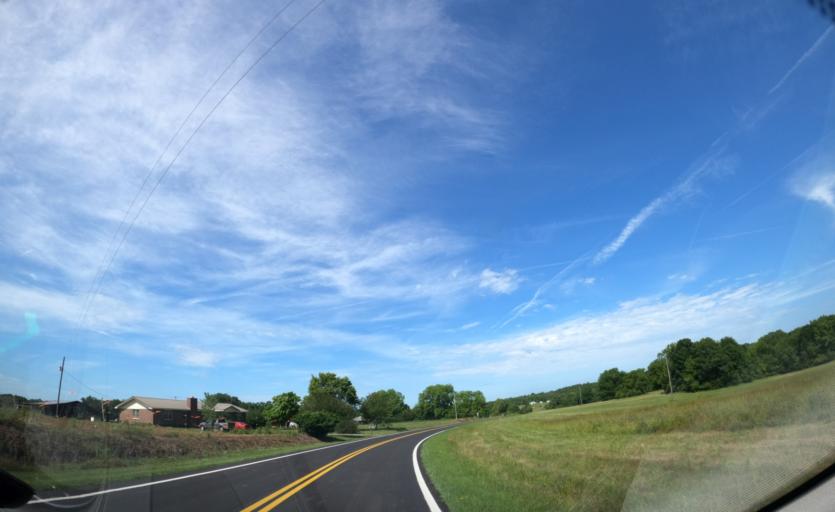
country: US
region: Georgia
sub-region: Elbert County
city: Elberton
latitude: 34.1131
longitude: -82.7394
